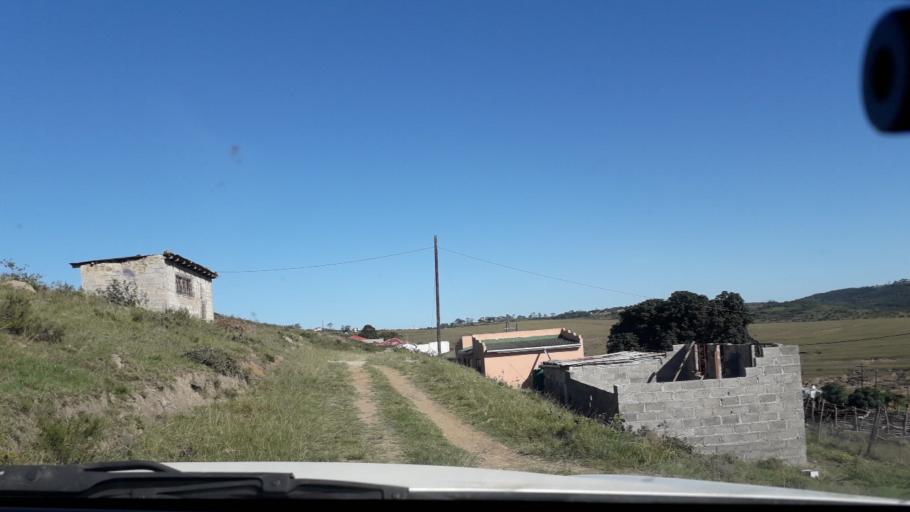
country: ZA
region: Eastern Cape
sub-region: Buffalo City Metropolitan Municipality
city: East London
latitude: -32.8381
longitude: 27.9972
